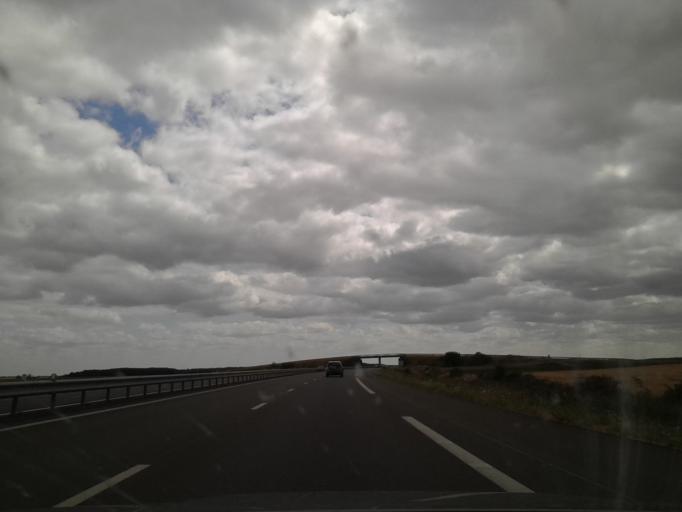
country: FR
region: Centre
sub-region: Departement du Cher
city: Levet
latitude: 46.9653
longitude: 2.4242
